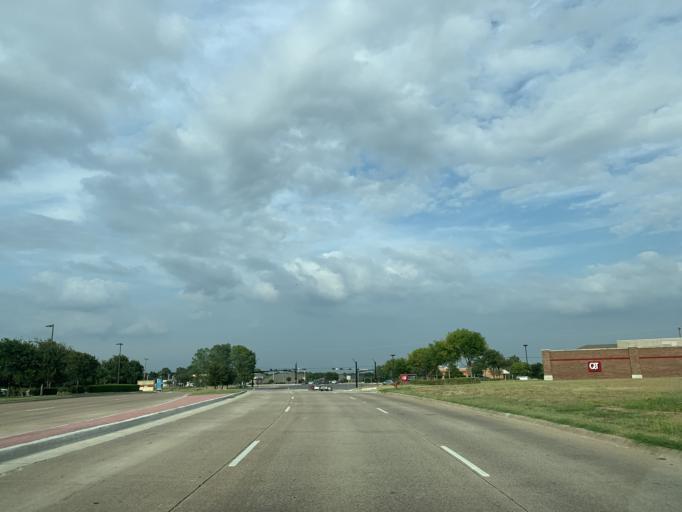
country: US
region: Texas
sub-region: Tarrant County
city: North Richland Hills
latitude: 32.8616
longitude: -97.2114
